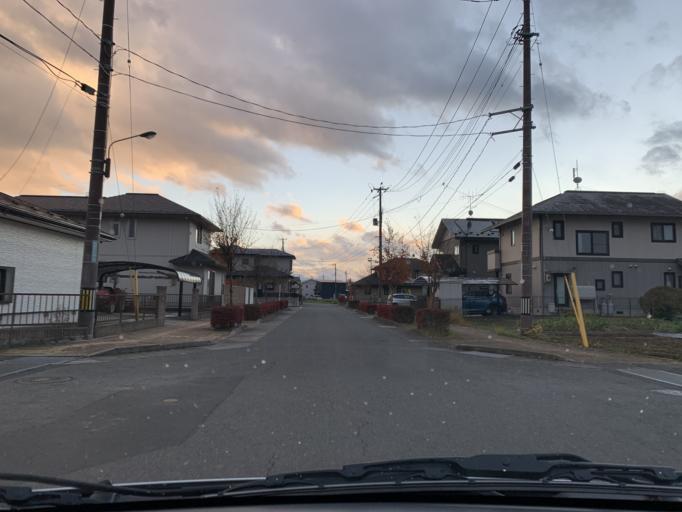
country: JP
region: Iwate
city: Mizusawa
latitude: 39.0520
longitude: 141.1276
